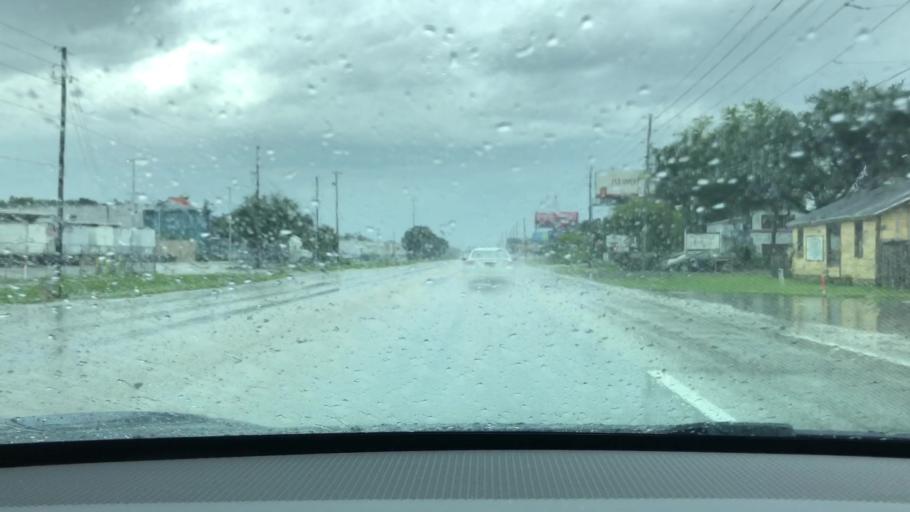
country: US
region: Florida
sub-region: Orange County
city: Belle Isle
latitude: 28.4581
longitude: -81.3656
